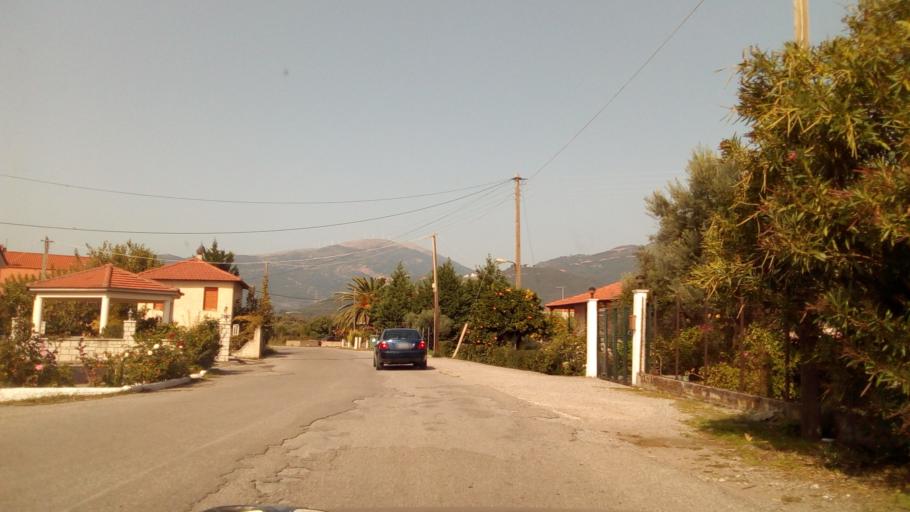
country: GR
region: West Greece
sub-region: Nomos Aitolias kai Akarnanias
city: Nafpaktos
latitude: 38.3952
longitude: 21.8829
